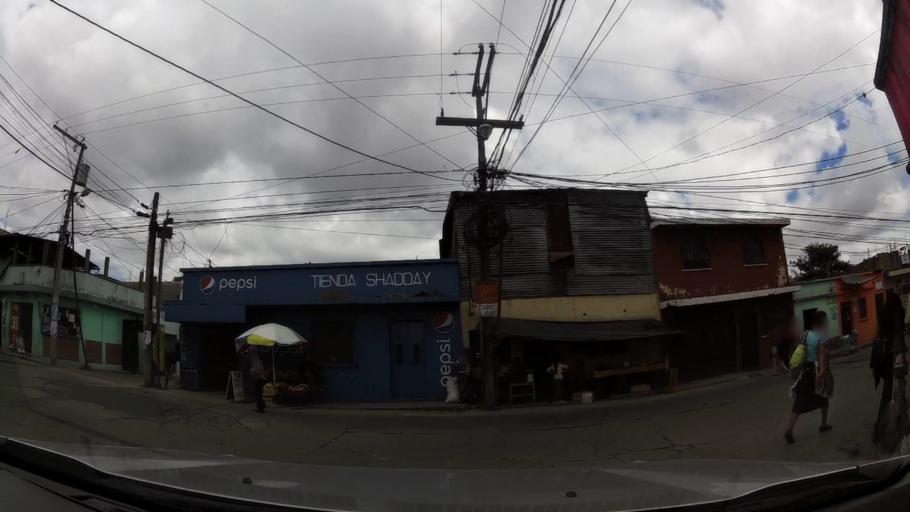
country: GT
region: Guatemala
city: Mixco
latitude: 14.6467
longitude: -90.5898
